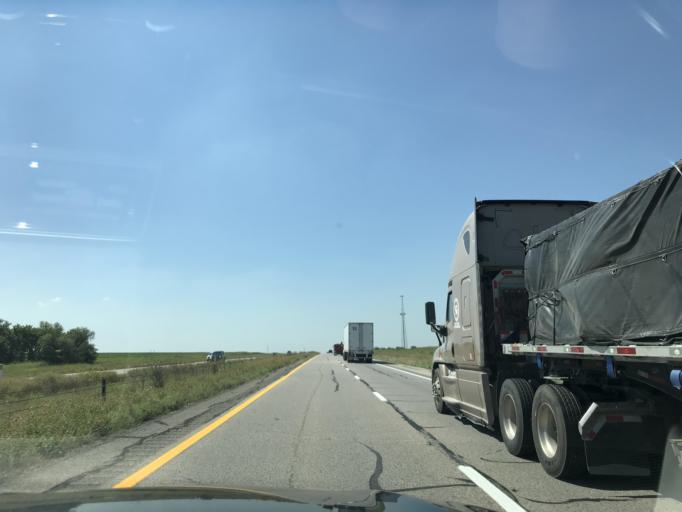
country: US
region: Texas
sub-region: Johnson County
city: Grandview
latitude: 32.3358
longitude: -97.1909
